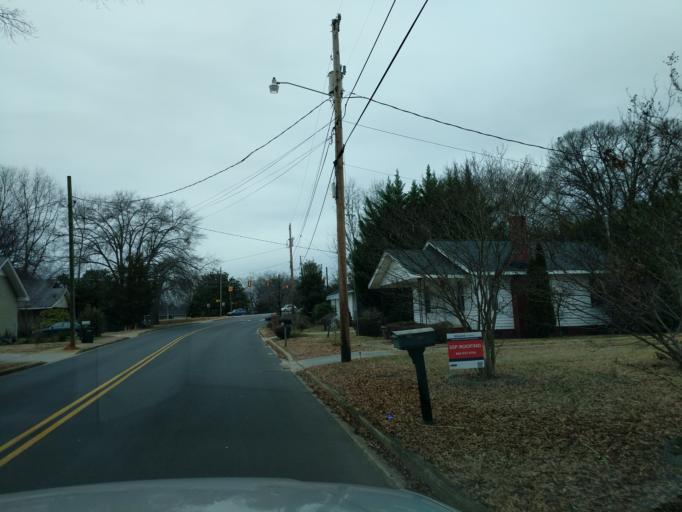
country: US
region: South Carolina
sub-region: Greenville County
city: Greer
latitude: 34.9324
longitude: -82.2295
